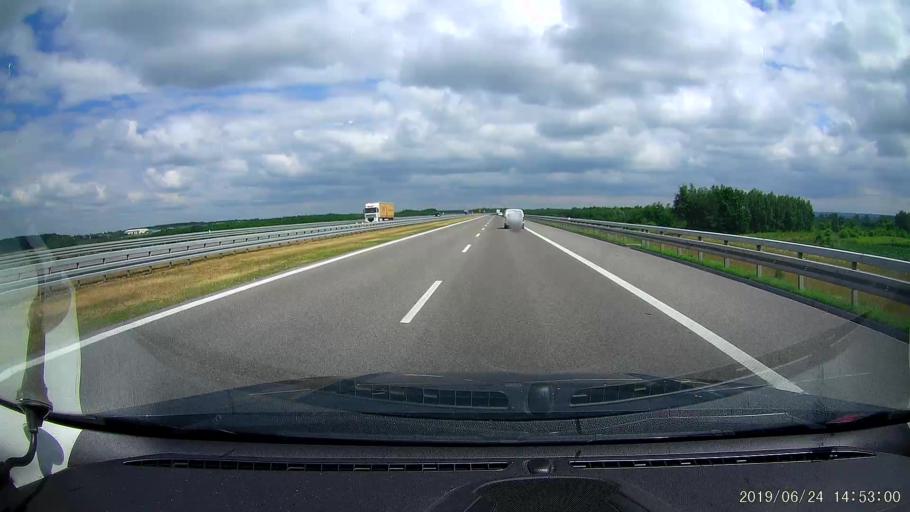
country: PL
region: Subcarpathian Voivodeship
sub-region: Powiat ropczycko-sedziszowski
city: Ostrow
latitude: 50.1065
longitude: 21.6027
